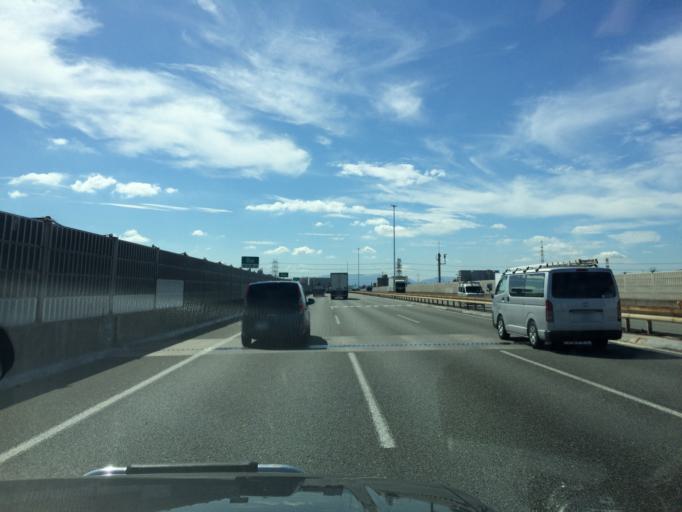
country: JP
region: Osaka
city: Yao
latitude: 34.6197
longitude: 135.5746
